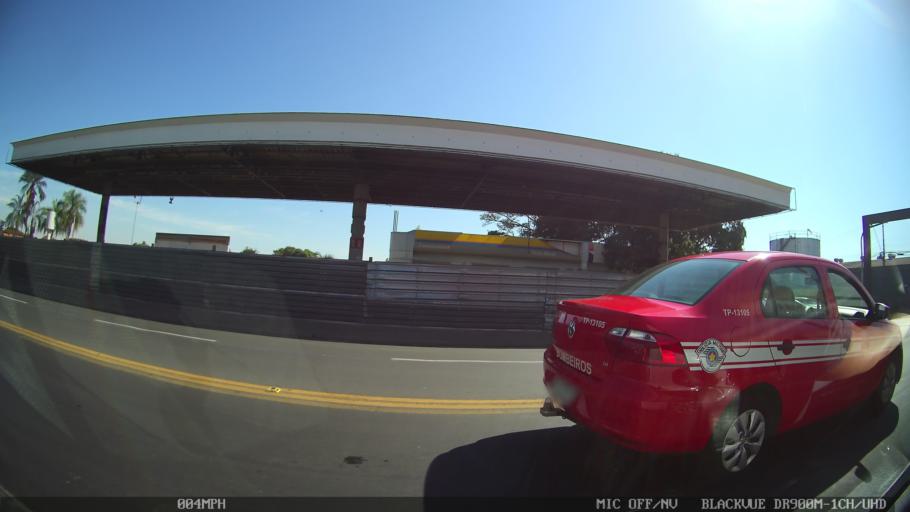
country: BR
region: Sao Paulo
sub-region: Sao Jose Do Rio Preto
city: Sao Jose do Rio Preto
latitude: -20.7954
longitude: -49.3909
